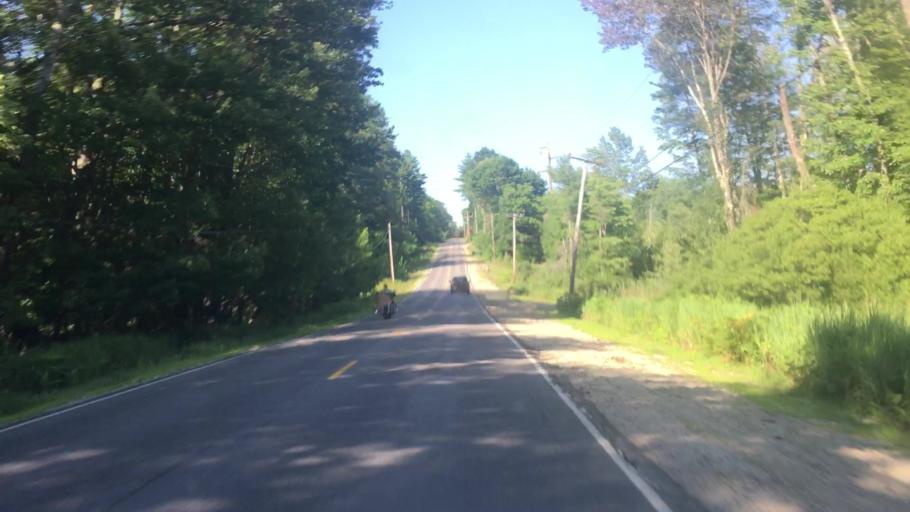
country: US
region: Maine
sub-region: York County
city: Buxton
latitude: 43.7063
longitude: -70.5774
